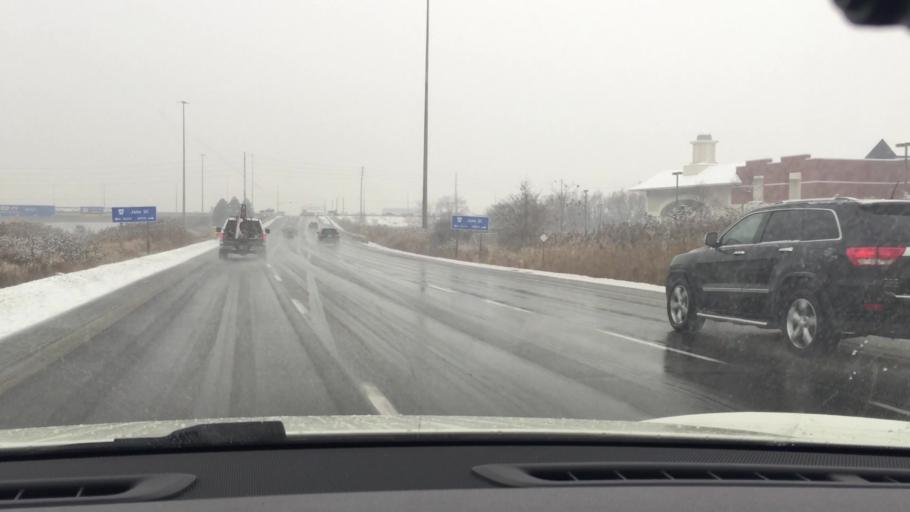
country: CA
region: Ontario
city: Concord
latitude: 43.7875
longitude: -79.5195
